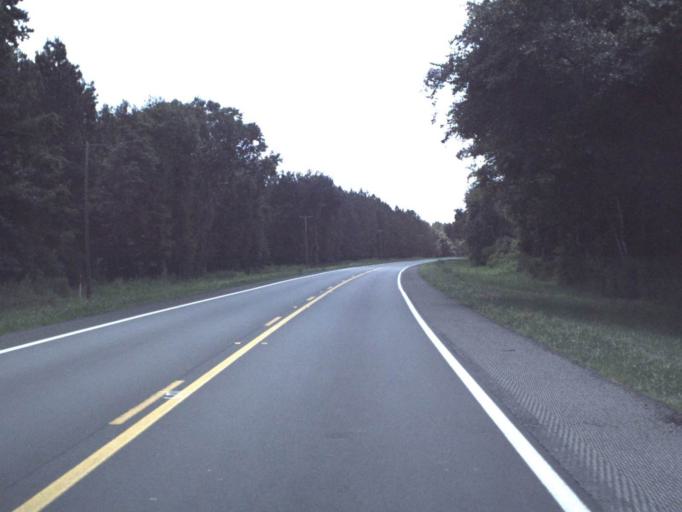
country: US
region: Florida
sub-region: Alachua County
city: Alachua
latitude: 29.8277
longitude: -82.3933
